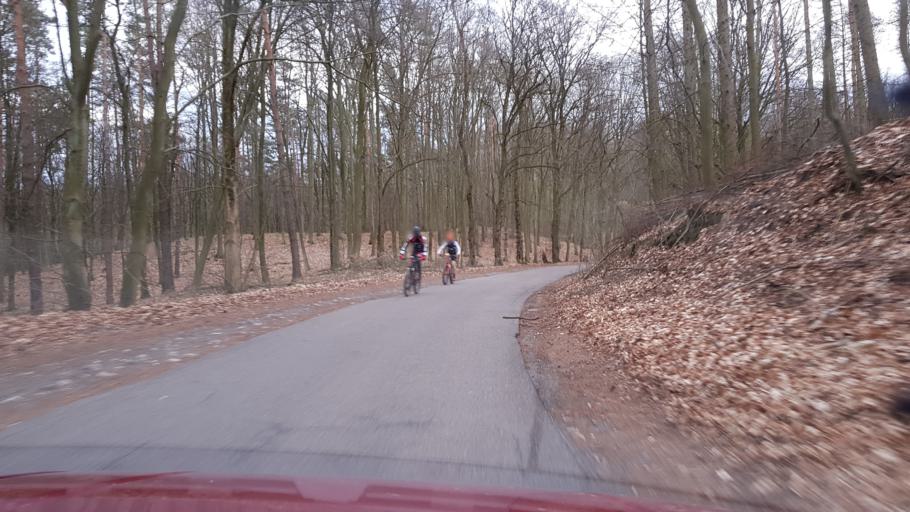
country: PL
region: West Pomeranian Voivodeship
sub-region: Szczecin
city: Szczecin
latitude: 53.3411
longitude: 14.6344
